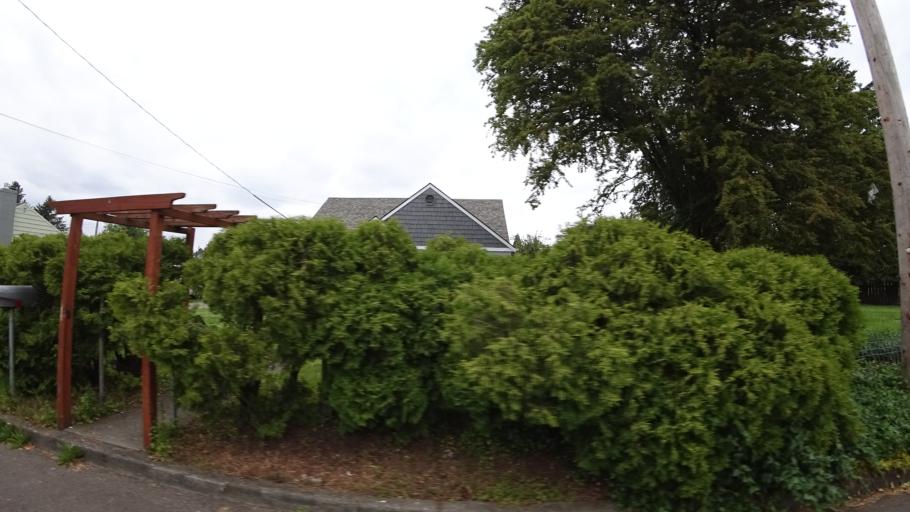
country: US
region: Oregon
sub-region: Multnomah County
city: Lents
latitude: 45.5091
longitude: -122.5354
